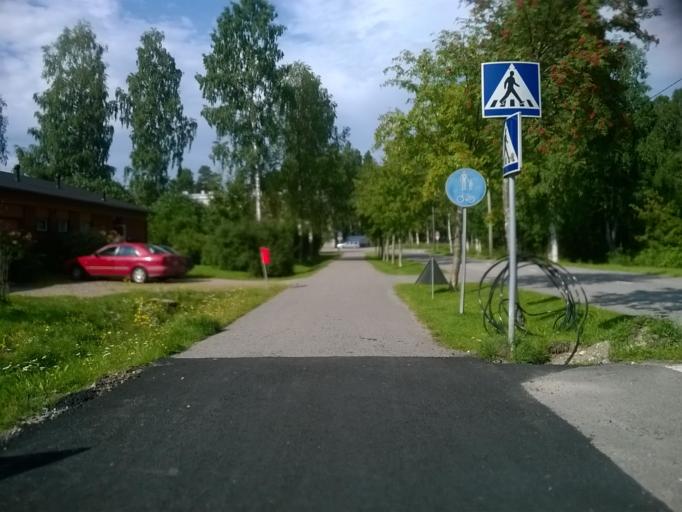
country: FI
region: Kainuu
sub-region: Kehys-Kainuu
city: Kuhmo
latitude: 64.1299
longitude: 29.5253
